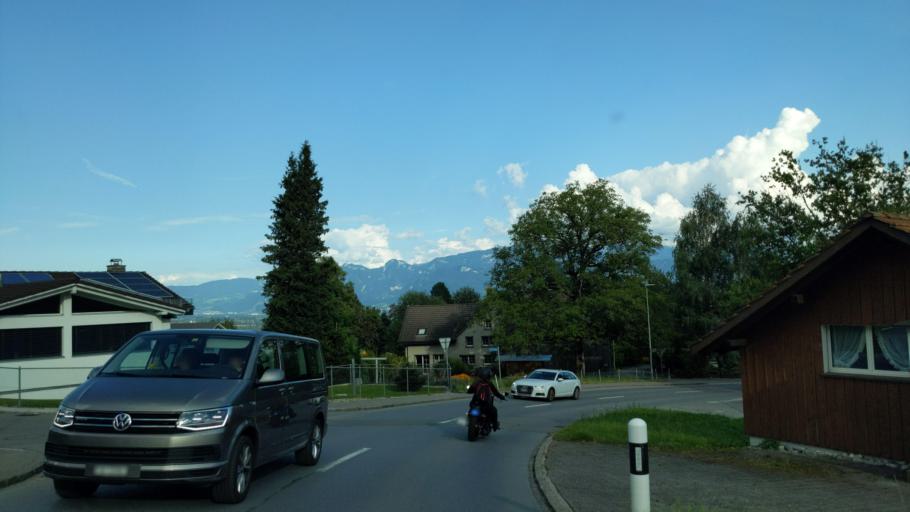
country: CH
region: Saint Gallen
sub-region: Wahlkreis Rheintal
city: Eichberg
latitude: 47.3431
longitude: 9.5172
